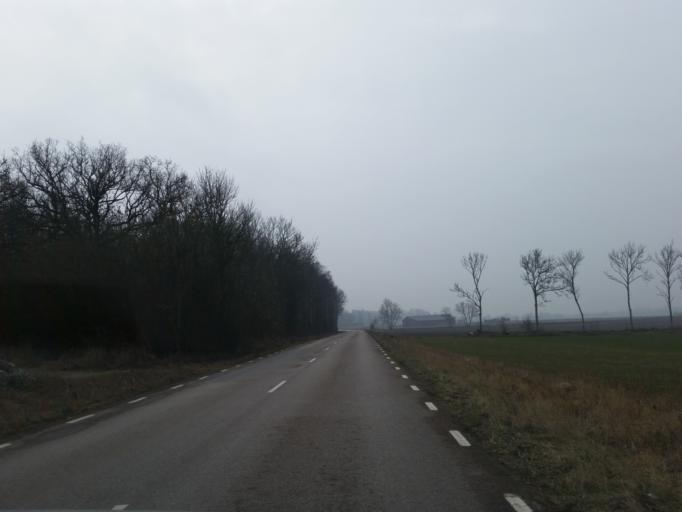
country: SE
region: Kalmar
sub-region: Morbylanga Kommun
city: Moerbylanga
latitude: 56.4386
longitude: 16.4213
